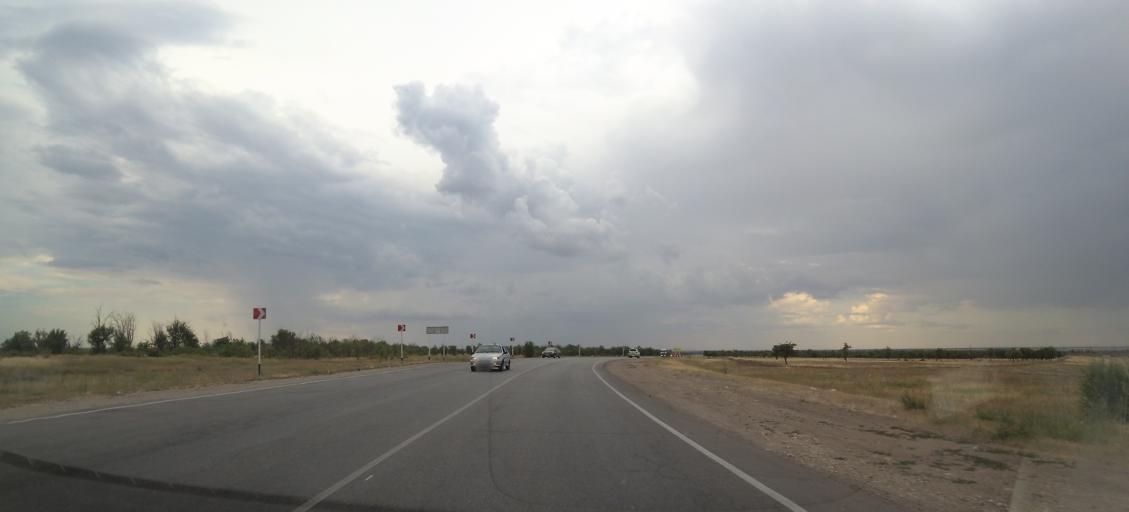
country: RU
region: Volgograd
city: Kotel'nikovo
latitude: 47.6103
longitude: 43.1064
